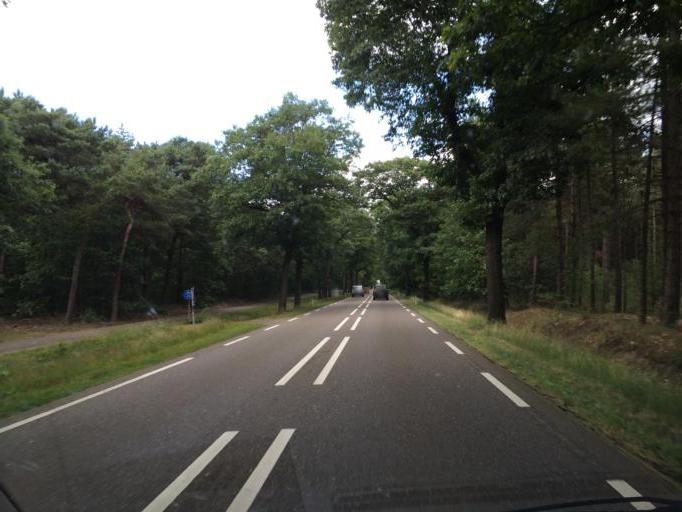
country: NL
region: North Brabant
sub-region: Bergeijk
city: Bergeyk
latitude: 51.2964
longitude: 5.4156
